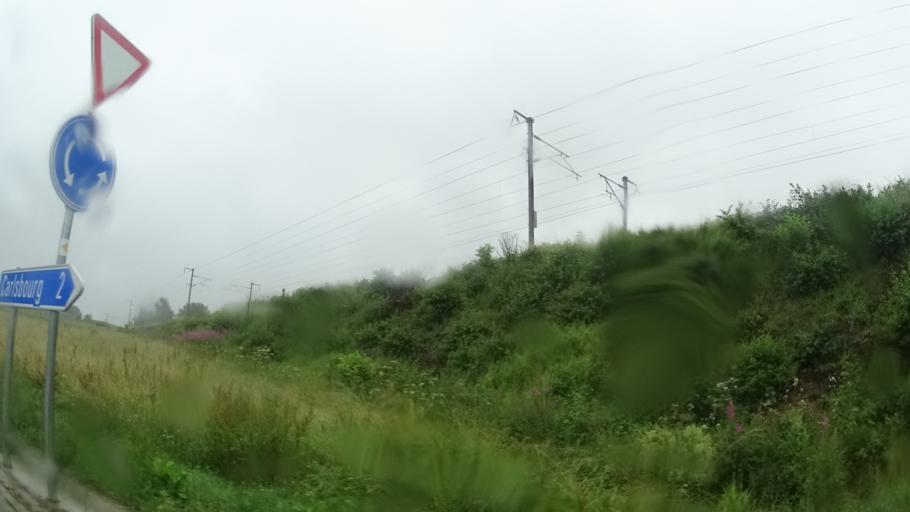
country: BE
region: Wallonia
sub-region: Province du Luxembourg
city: Paliseul
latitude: 49.9017
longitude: 5.1039
